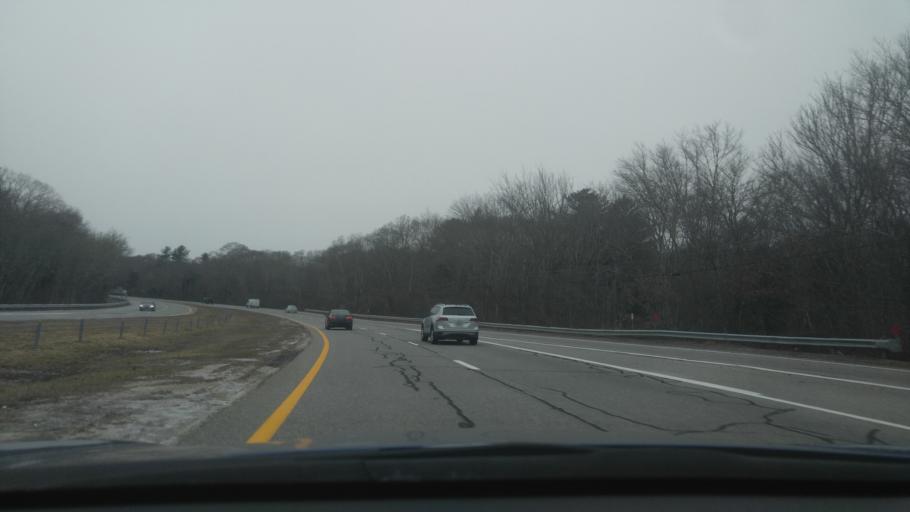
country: US
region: Rhode Island
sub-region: Washington County
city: Wakefield-Peacedale
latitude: 41.4274
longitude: -71.5199
